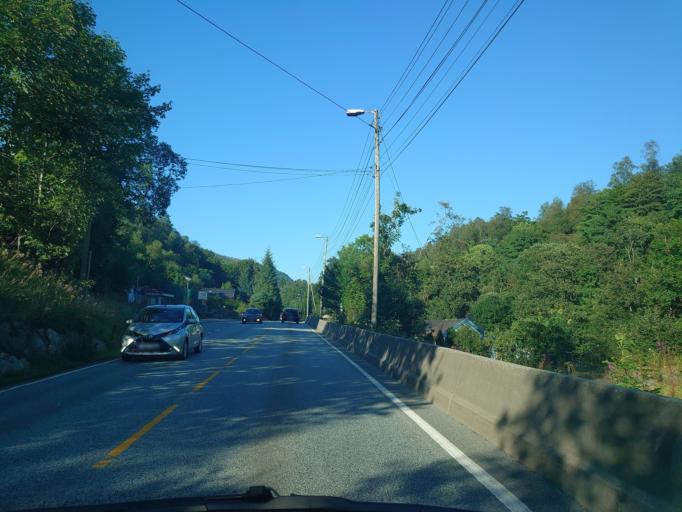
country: NO
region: Hordaland
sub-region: Bergen
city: Bergen
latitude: 60.3332
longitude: 5.3894
